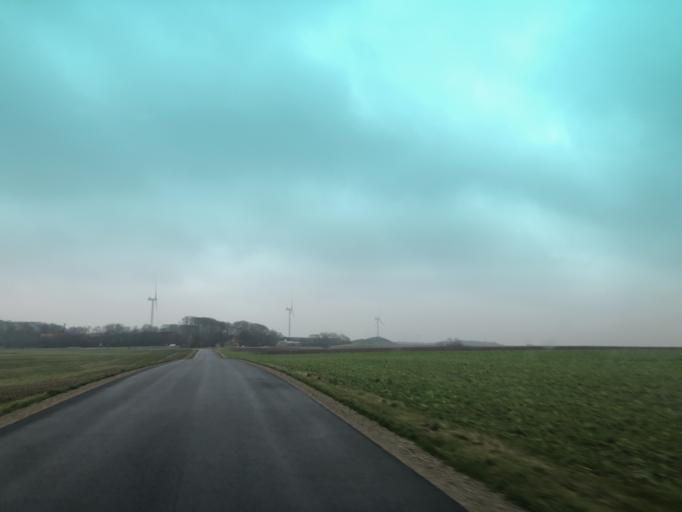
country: DK
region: Central Jutland
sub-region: Struer Kommune
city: Struer
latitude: 56.4316
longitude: 8.5925
